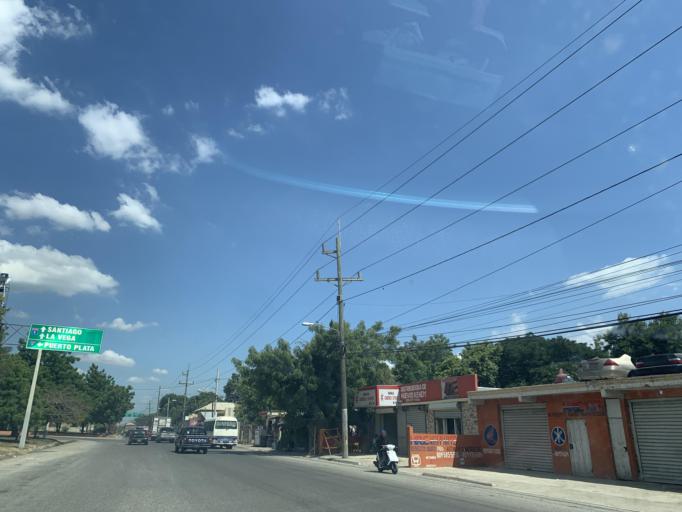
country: DO
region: Santiago
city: Villa Bisono
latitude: 19.5550
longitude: -70.8611
